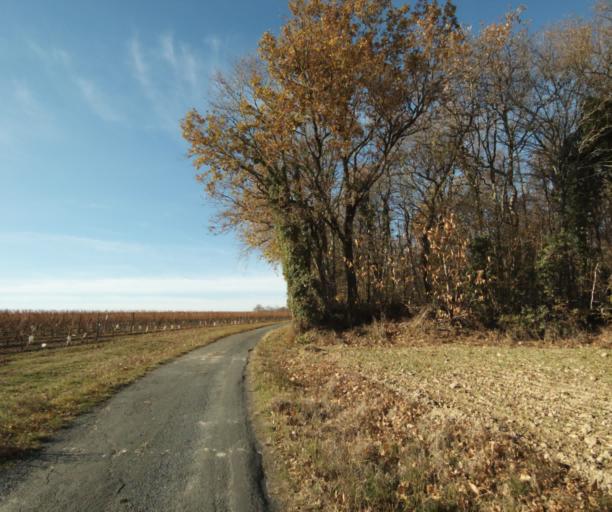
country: FR
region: Poitou-Charentes
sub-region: Departement de la Charente-Maritime
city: Chaniers
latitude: 45.7554
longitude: -0.5111
